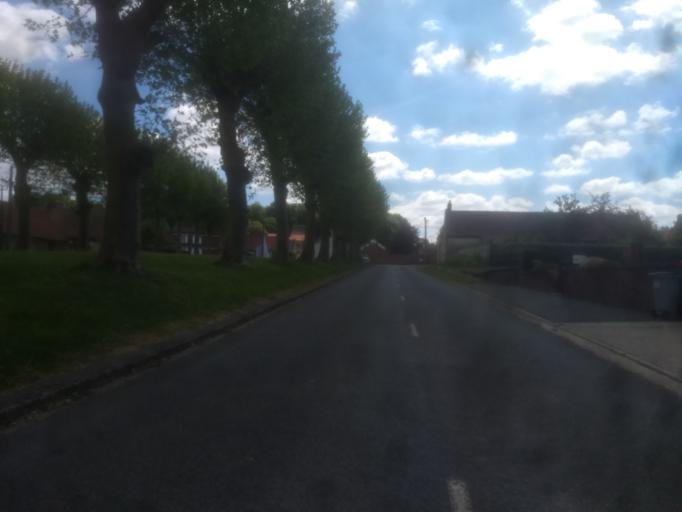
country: FR
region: Nord-Pas-de-Calais
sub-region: Departement du Pas-de-Calais
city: Riviere
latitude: 50.2298
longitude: 2.6788
